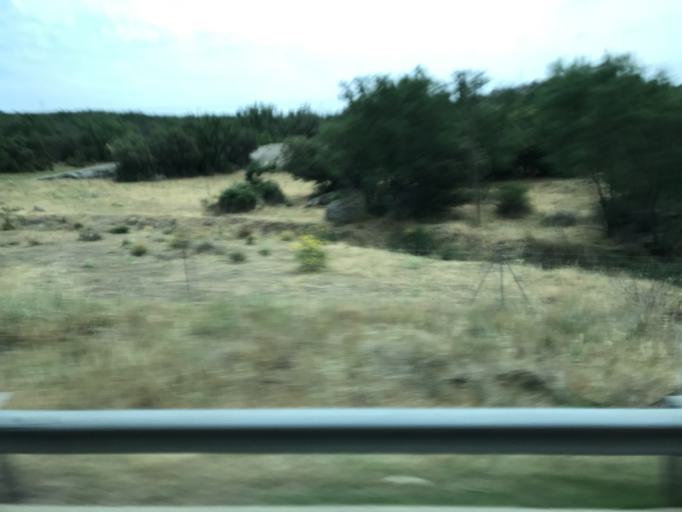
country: ES
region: Madrid
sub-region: Provincia de Madrid
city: La Cabrera
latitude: 40.8683
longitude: -3.6055
